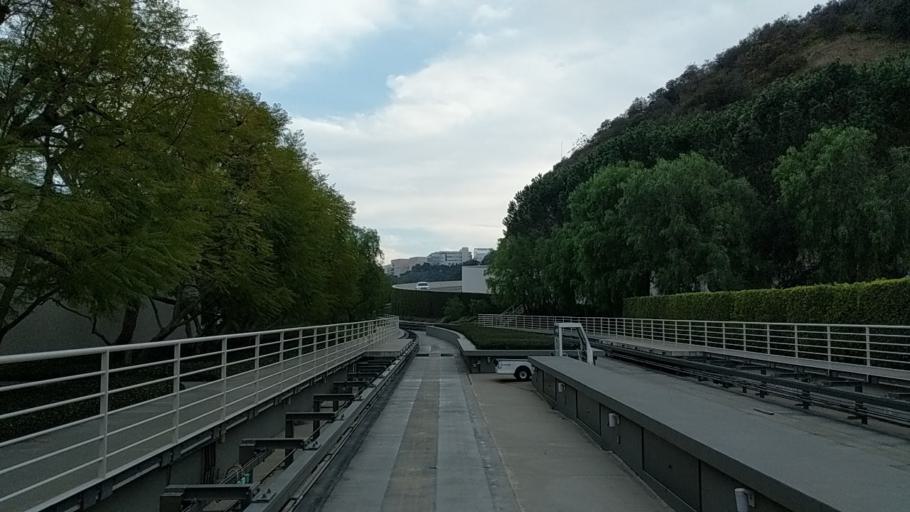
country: US
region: California
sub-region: Los Angeles County
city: Westwood, Los Angeles
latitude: 34.0873
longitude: -118.4757
